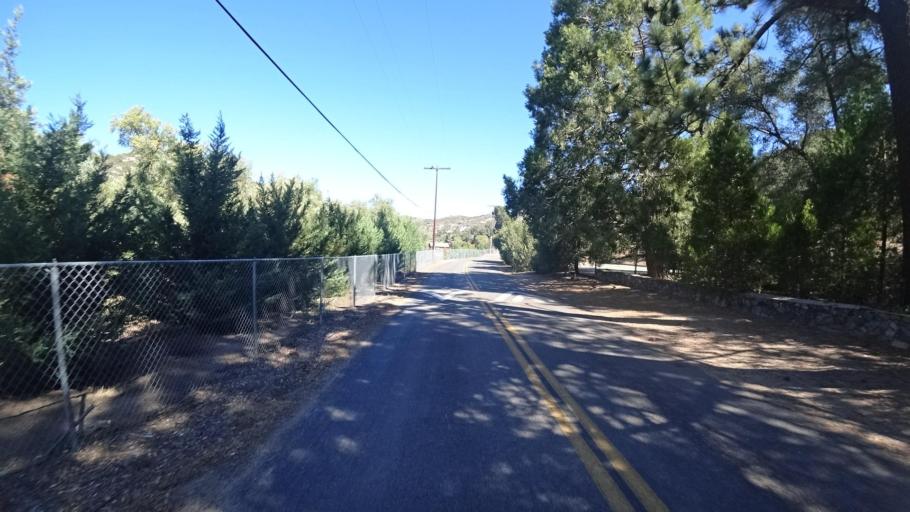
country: US
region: California
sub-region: San Diego County
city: Descanso
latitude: 32.8682
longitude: -116.6220
